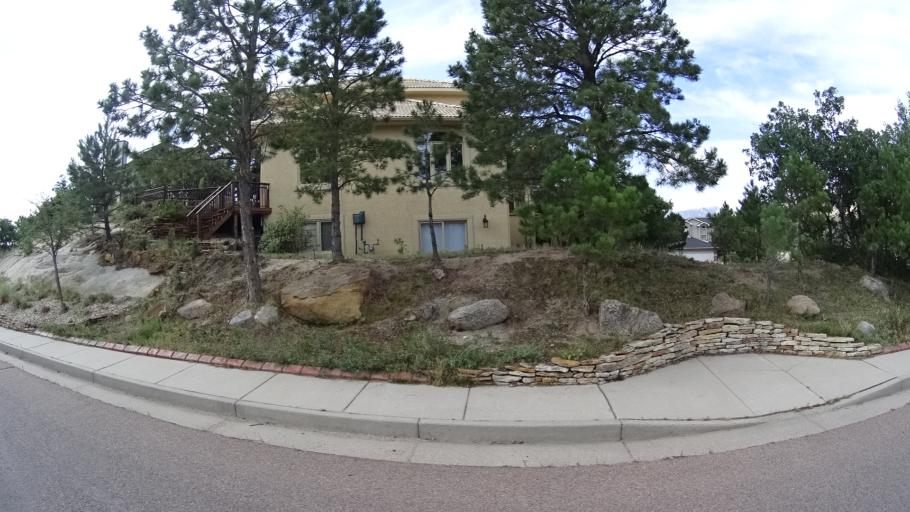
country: US
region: Colorado
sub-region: El Paso County
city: Air Force Academy
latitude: 38.9474
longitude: -104.8626
